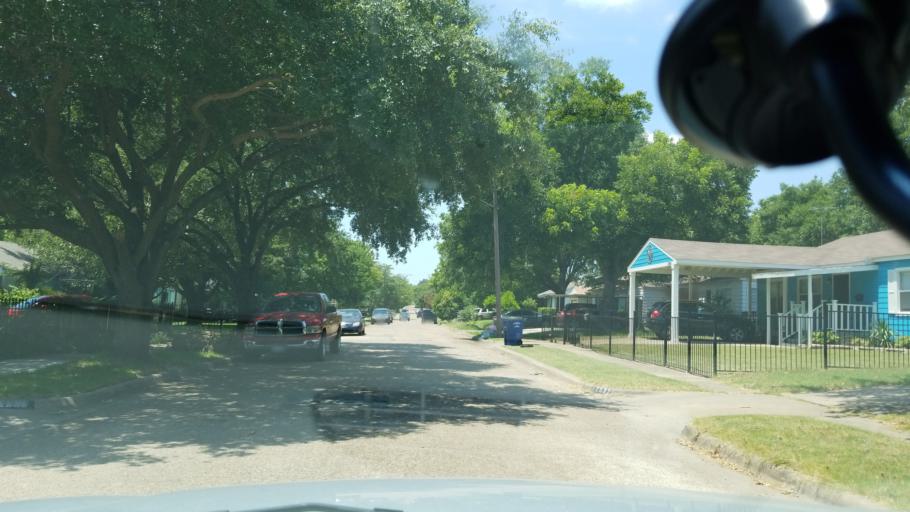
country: US
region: Texas
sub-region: Dallas County
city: Cockrell Hill
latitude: 32.7242
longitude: -96.8612
